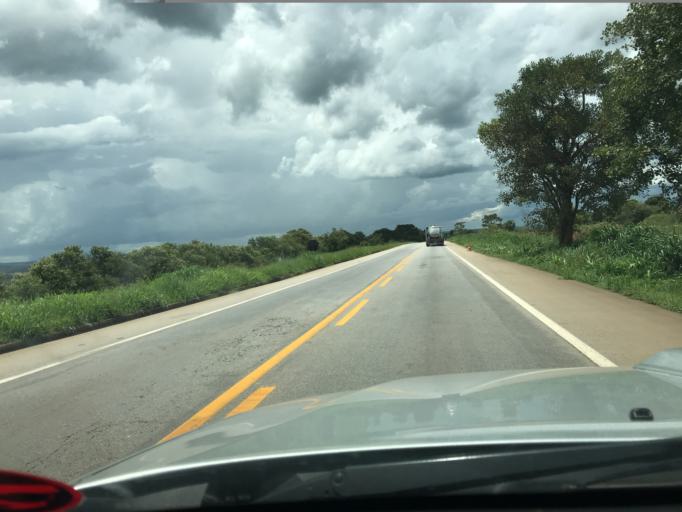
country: BR
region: Minas Gerais
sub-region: Ibia
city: Ibia
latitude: -19.5865
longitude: -46.4640
